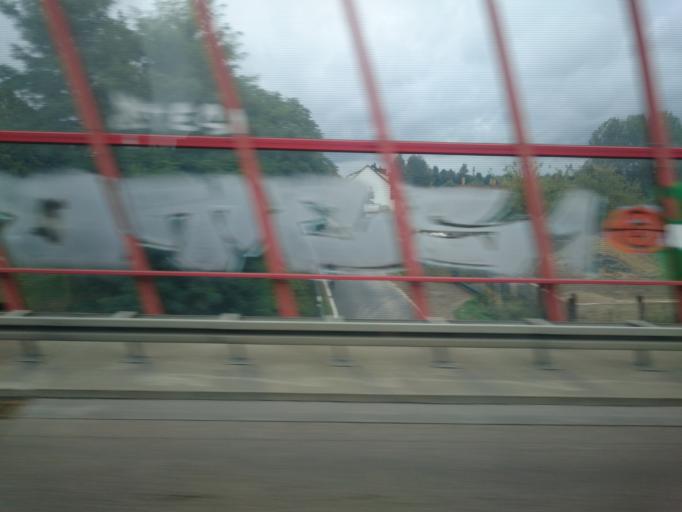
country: DE
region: Saxony-Anhalt
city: Ermlitz
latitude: 51.3900
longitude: 12.1814
